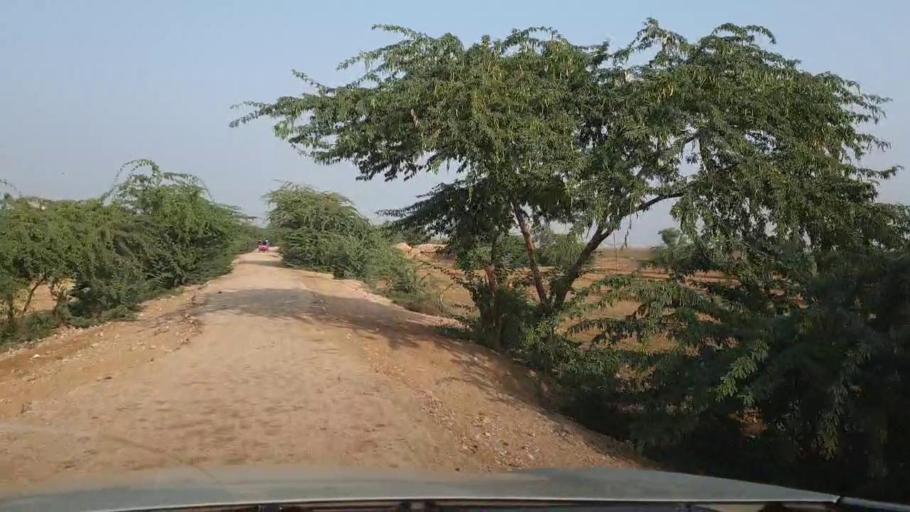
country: PK
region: Sindh
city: Sehwan
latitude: 26.3448
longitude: 67.7242
